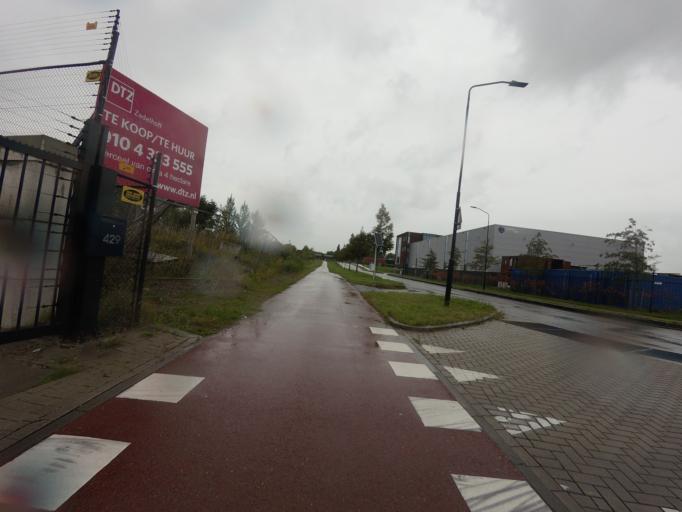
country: NL
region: South Holland
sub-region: Gemeente Alblasserdam
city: Alblasserdam
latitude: 51.8467
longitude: 4.6709
